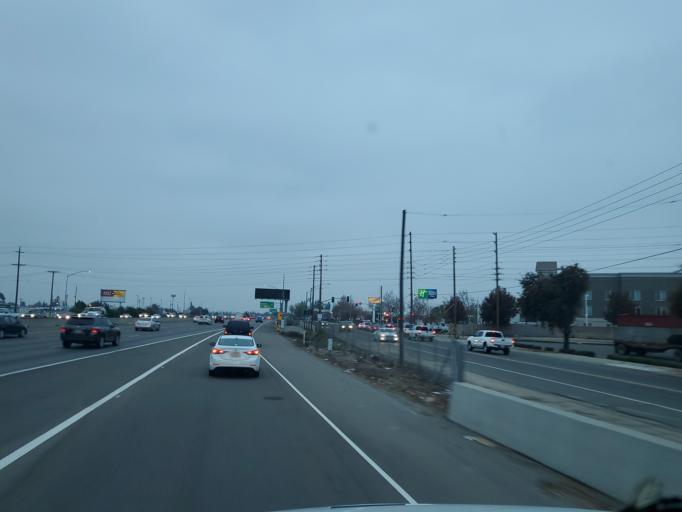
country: US
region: California
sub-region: Stanislaus County
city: Salida
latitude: 37.7029
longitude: -121.0737
